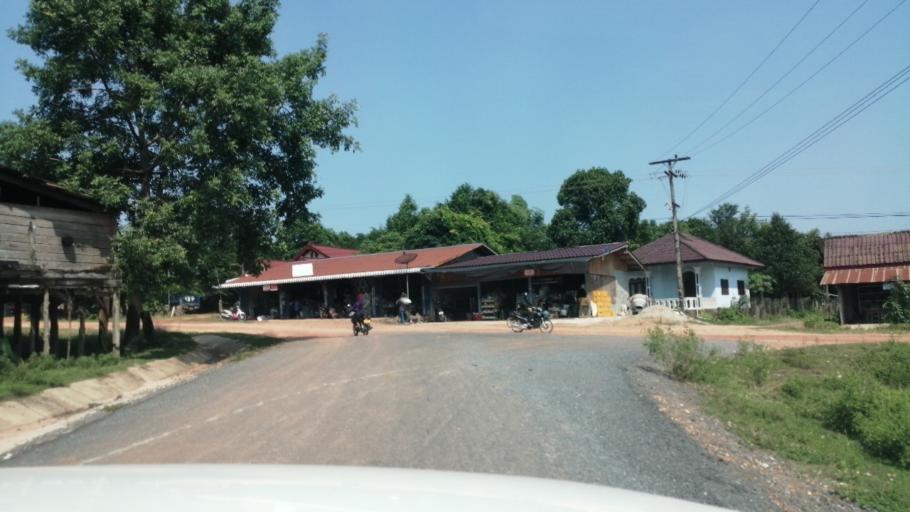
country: LA
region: Bolikhamxai
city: Bolikhan
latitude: 18.4610
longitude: 103.7956
